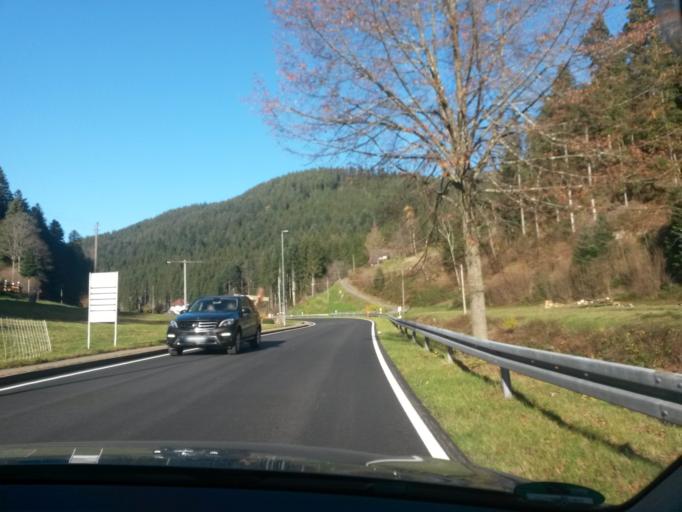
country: DE
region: Baden-Wuerttemberg
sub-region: Karlsruhe Region
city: Bad Rippoldsau-Schapbach
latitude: 48.4395
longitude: 8.3146
